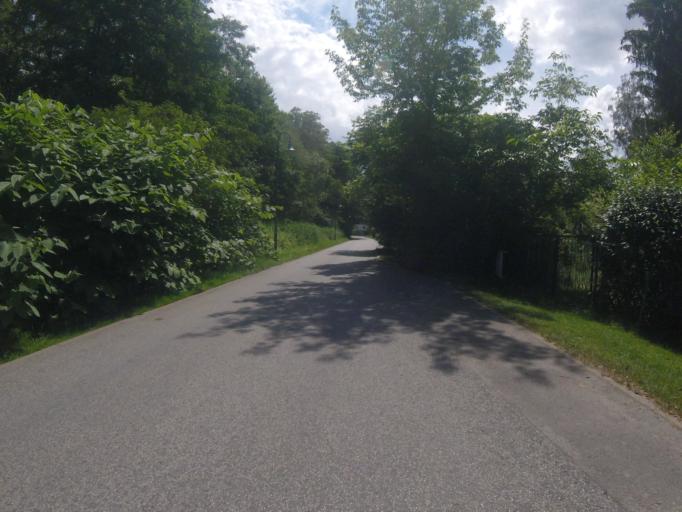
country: DE
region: Brandenburg
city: Bestensee
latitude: 52.2684
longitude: 13.6415
